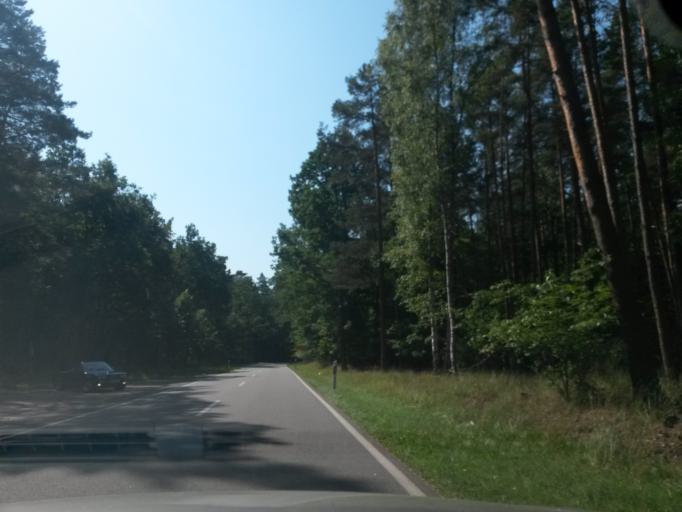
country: DE
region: Brandenburg
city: Marienwerder
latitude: 52.9014
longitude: 13.6442
